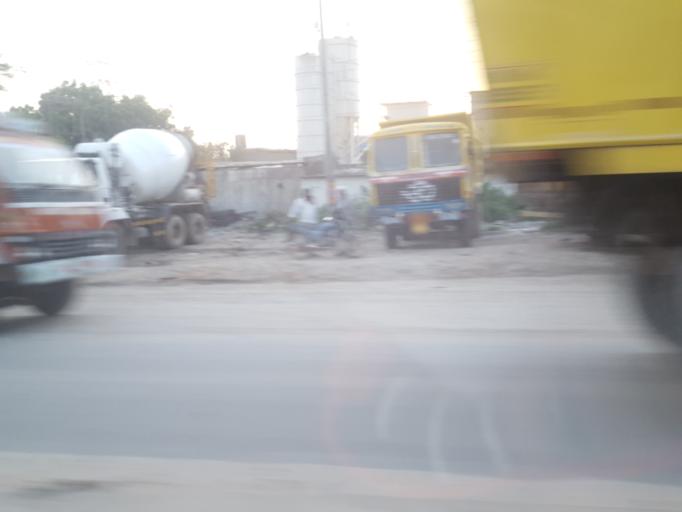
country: IN
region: Telangana
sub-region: Medak
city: Serilingampalle
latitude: 17.5351
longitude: 78.3580
